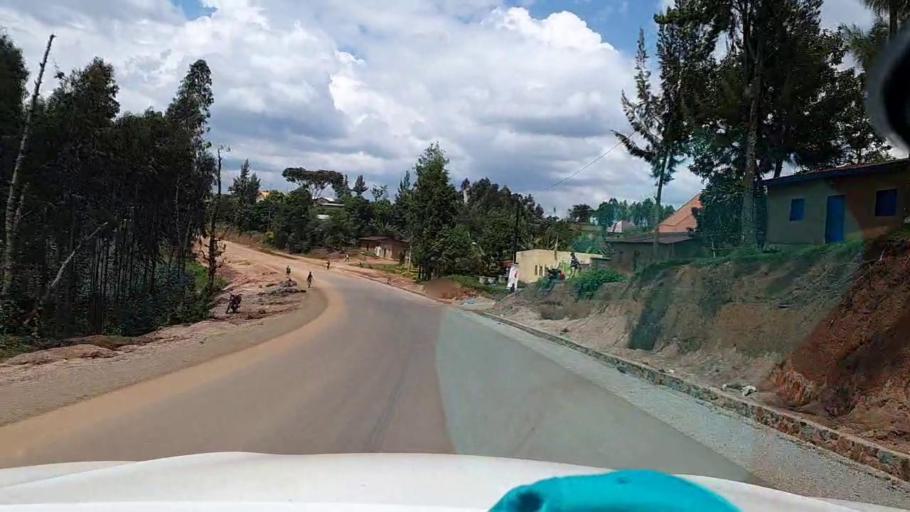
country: RW
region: Southern Province
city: Nzega
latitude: -2.6469
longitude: 29.5666
